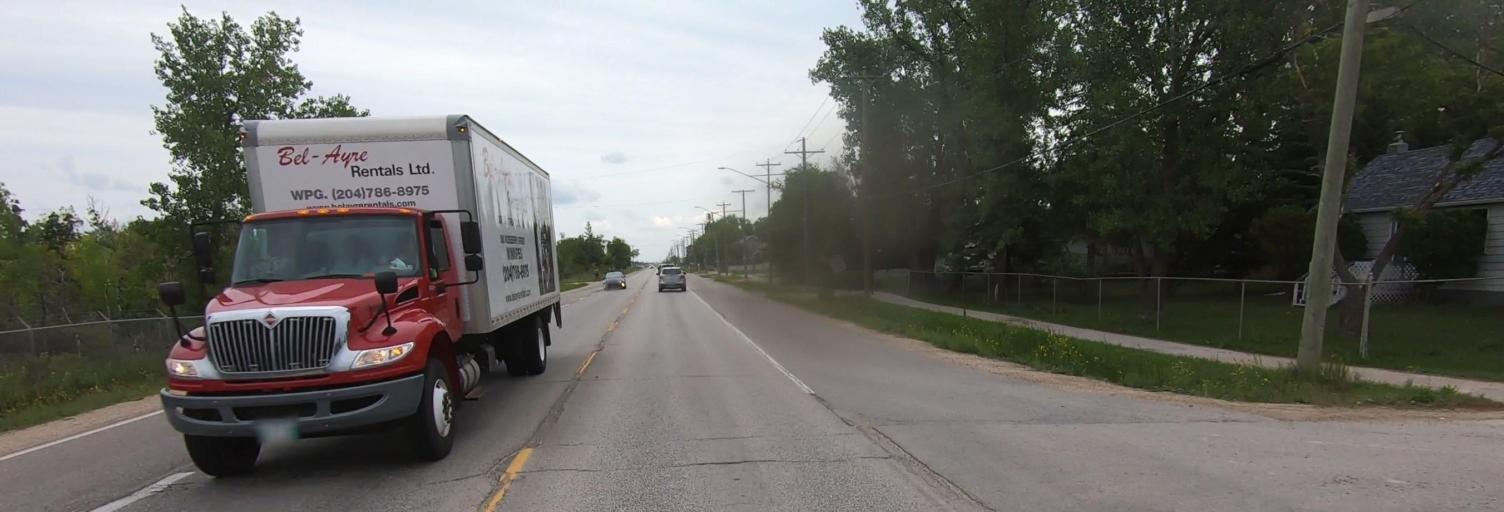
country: CA
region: Manitoba
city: Winnipeg
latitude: 49.8152
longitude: -97.2192
